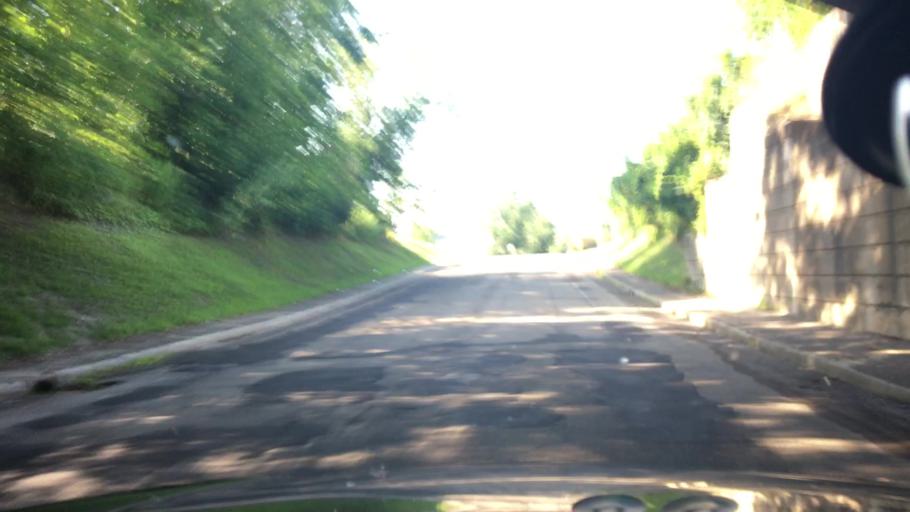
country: US
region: New York
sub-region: Erie County
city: Angola
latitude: 42.6318
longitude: -79.0277
